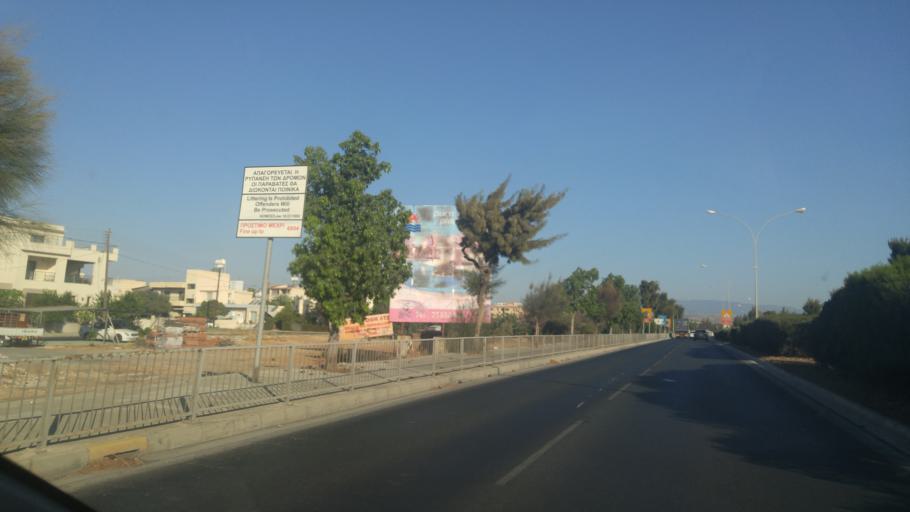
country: CY
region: Limassol
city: Limassol
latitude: 34.6778
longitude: 33.0107
